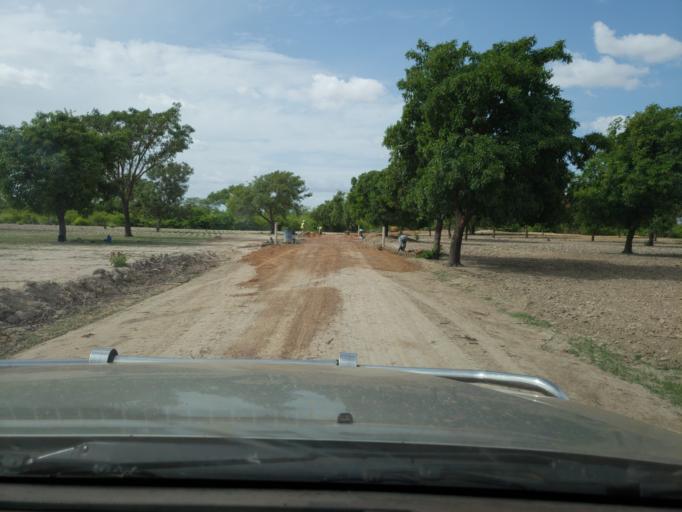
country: ML
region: Segou
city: Bla
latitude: 12.7696
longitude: -5.6179
